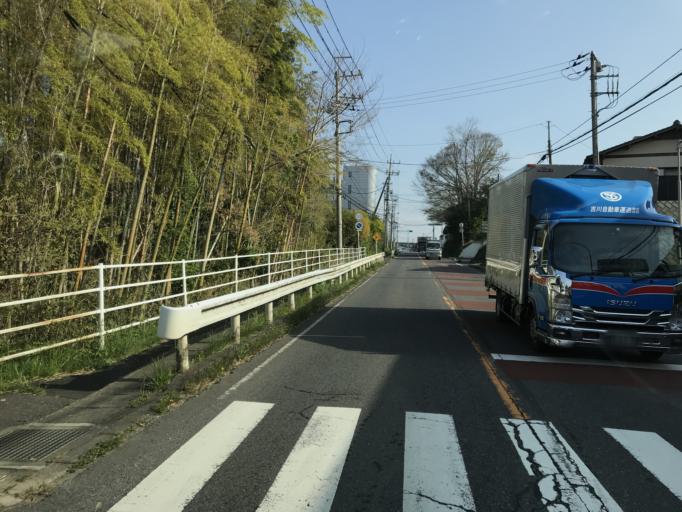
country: JP
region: Chiba
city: Narita
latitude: 35.7571
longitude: 140.3041
